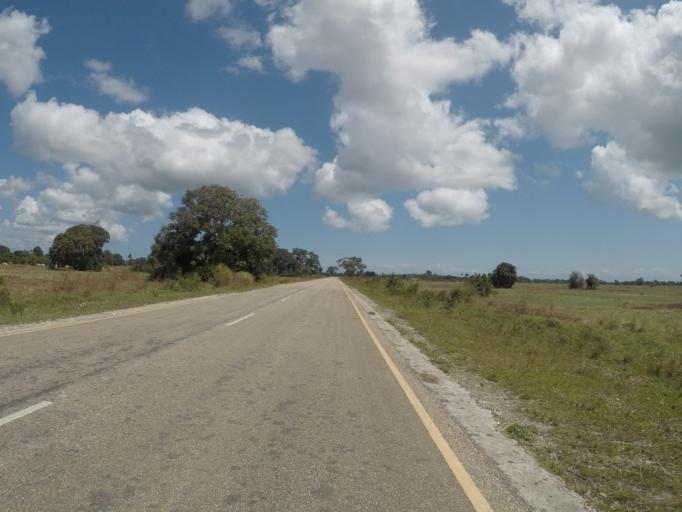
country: TZ
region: Zanzibar Central/South
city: Koani
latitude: -6.2111
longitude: 39.3658
